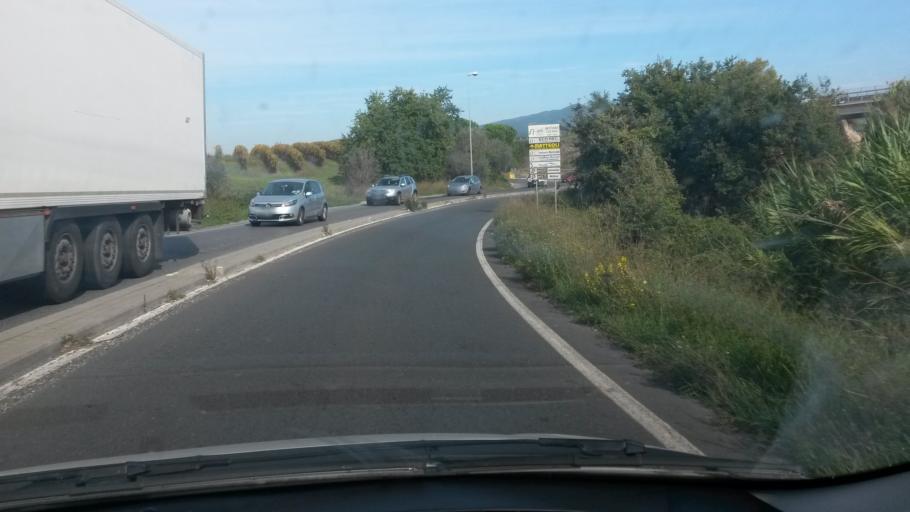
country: IT
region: Tuscany
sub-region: Provincia di Livorno
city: Cecina
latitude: 43.3167
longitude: 10.5329
